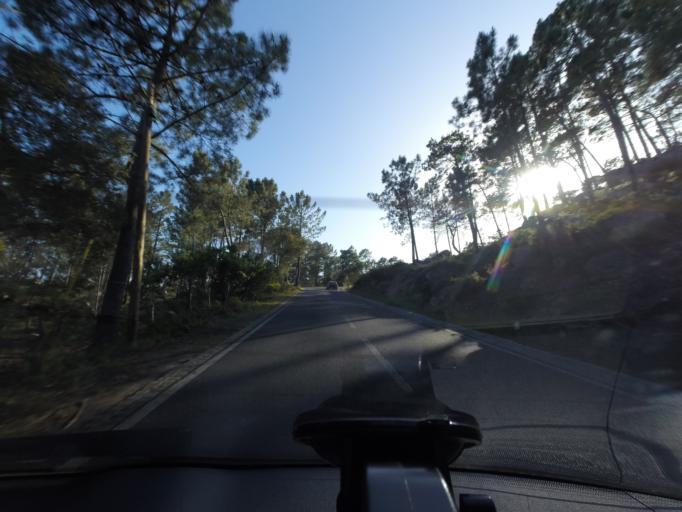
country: PT
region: Lisbon
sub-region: Cascais
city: Alcabideche
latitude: 38.7559
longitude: -9.4268
